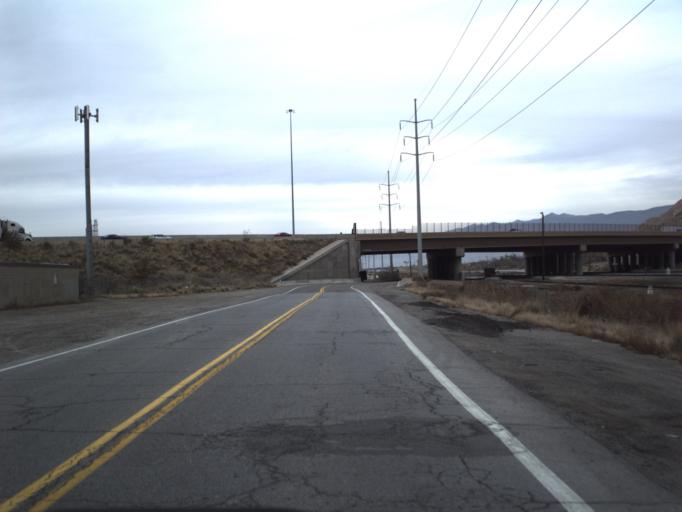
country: US
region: Utah
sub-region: Davis County
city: North Salt Lake
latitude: 40.8141
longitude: -111.9206
